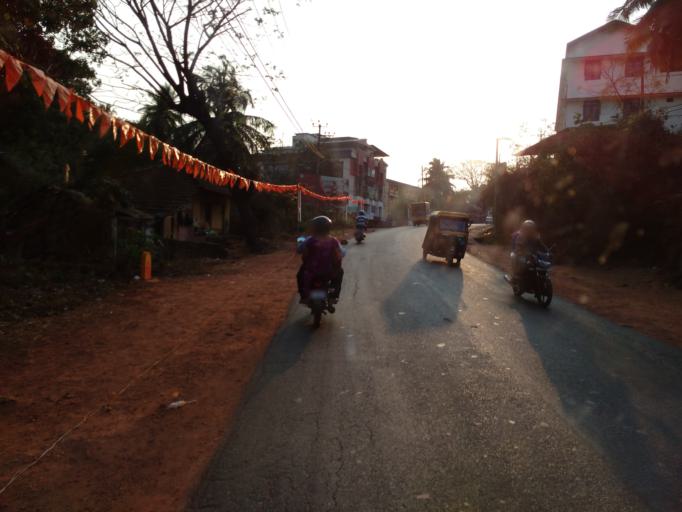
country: IN
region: Karnataka
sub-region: Dakshina Kannada
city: Mangalore
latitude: 12.8859
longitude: 74.8846
